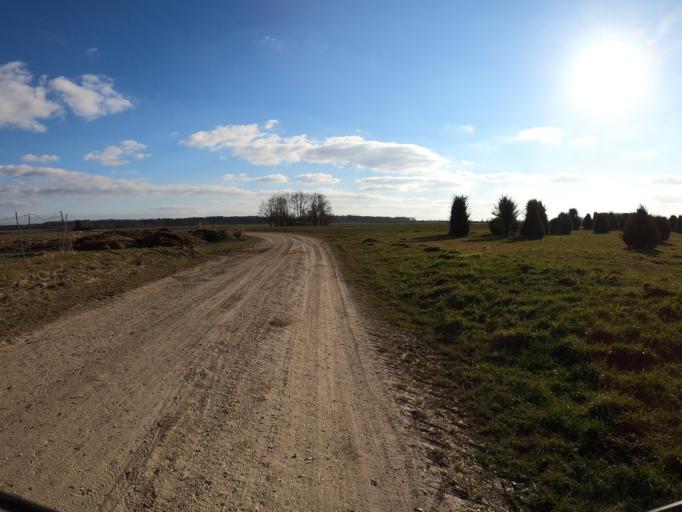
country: DE
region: Bavaria
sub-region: Swabia
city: Leipheim
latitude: 48.4358
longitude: 10.2126
